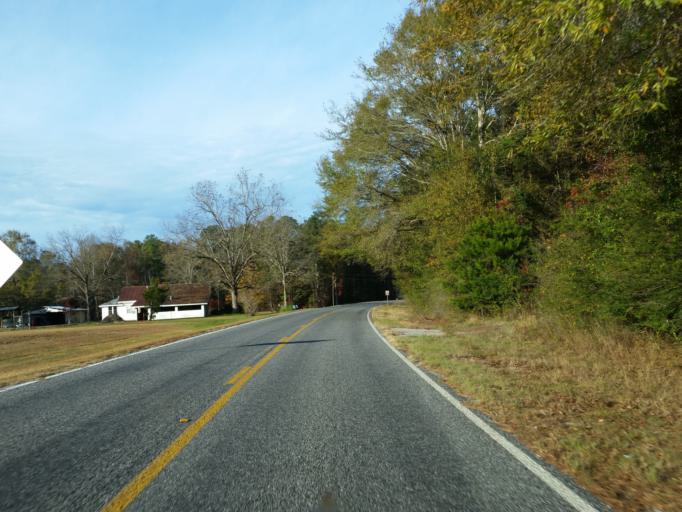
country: US
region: Mississippi
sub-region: Clarke County
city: Stonewall
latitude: 32.0697
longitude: -88.8792
